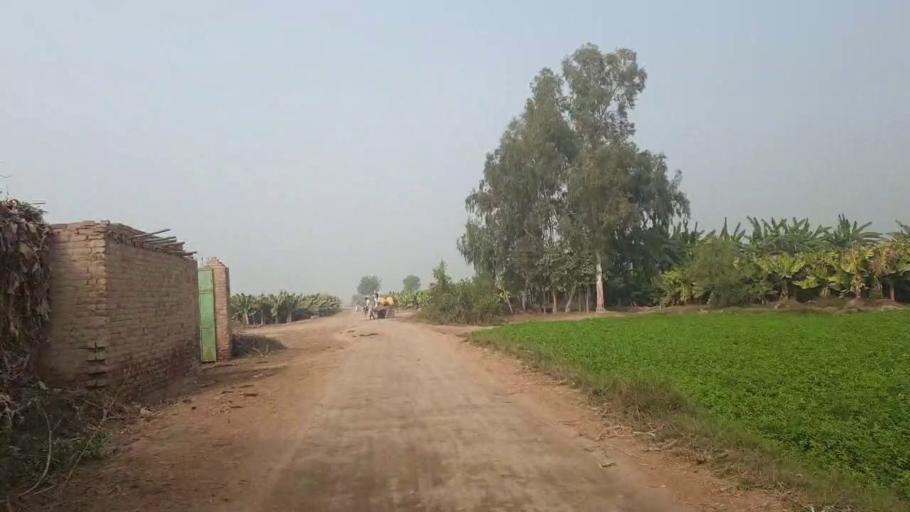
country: PK
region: Sindh
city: Bhit Shah
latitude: 25.8124
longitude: 68.5784
